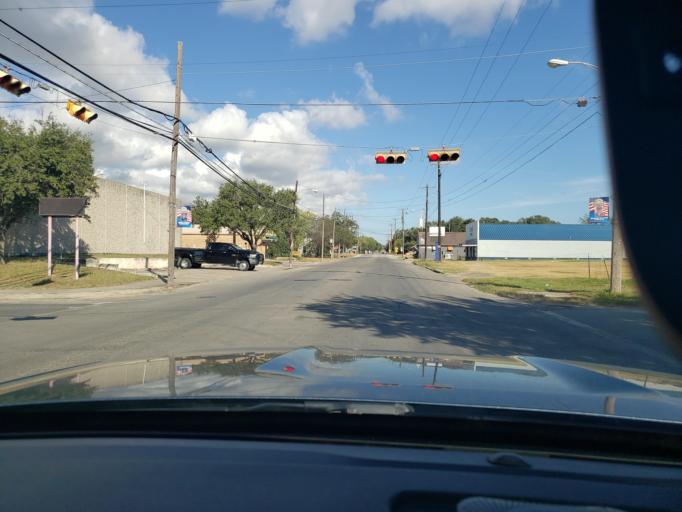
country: US
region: Texas
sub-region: Bee County
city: Beeville
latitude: 28.4049
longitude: -97.7498
